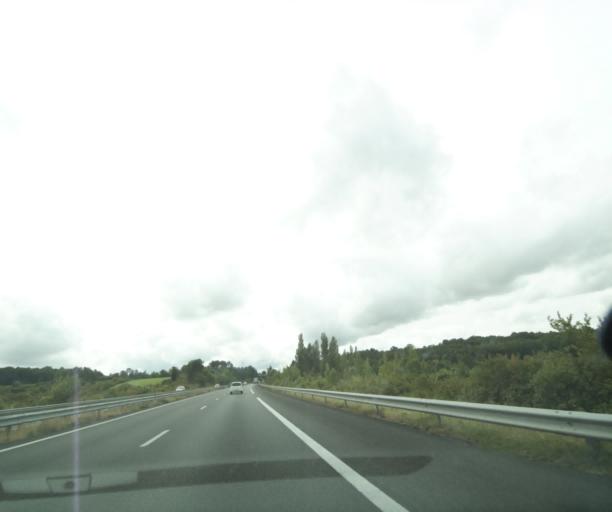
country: FR
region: Poitou-Charentes
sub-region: Departement de la Charente-Maritime
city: Mirambeau
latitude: 45.4105
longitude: -0.6015
